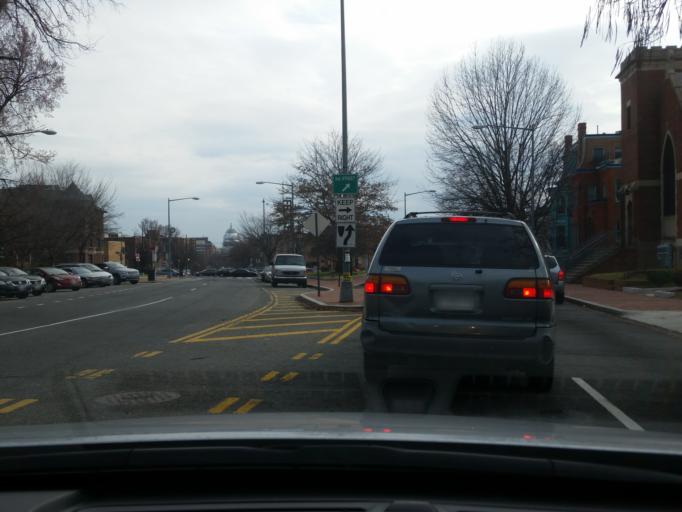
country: US
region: Washington, D.C.
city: Washington, D.C.
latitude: 38.9066
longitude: -77.0152
